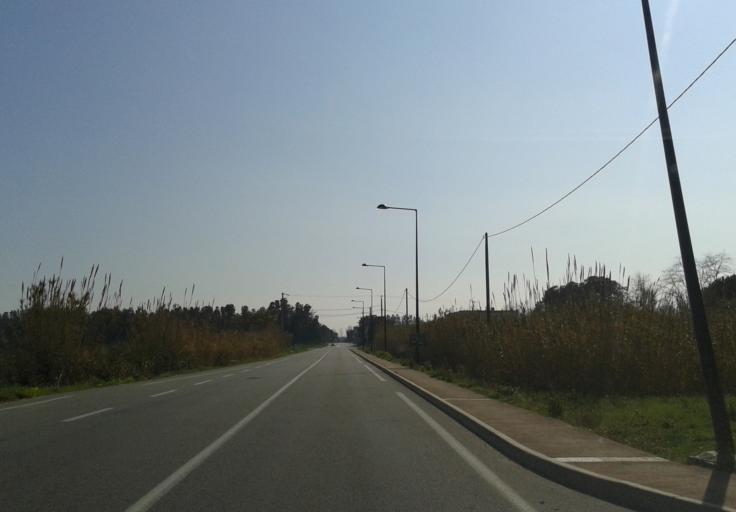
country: FR
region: Corsica
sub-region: Departement de la Haute-Corse
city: Linguizzetta
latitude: 42.2586
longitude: 9.5471
